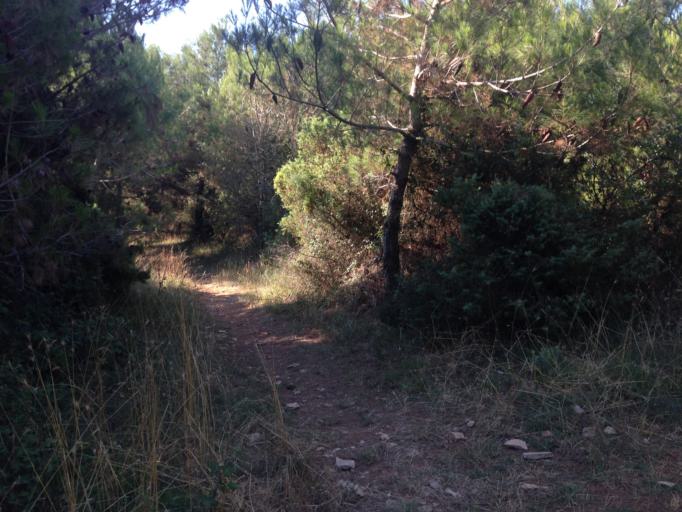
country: HR
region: Istarska
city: Medulin
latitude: 44.7946
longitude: 13.9075
